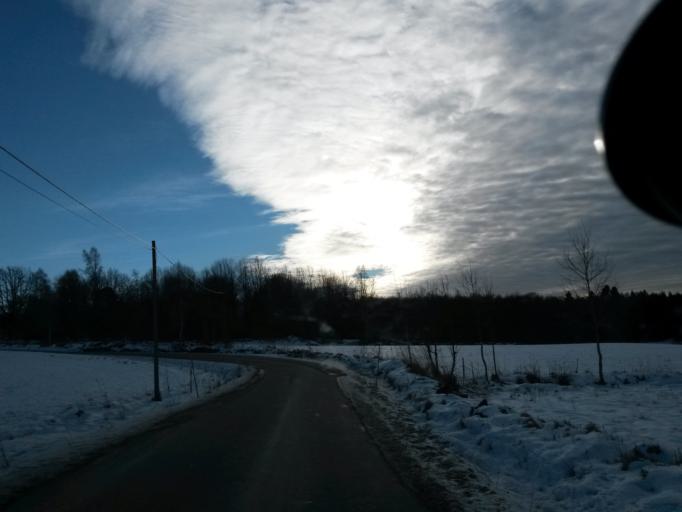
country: SE
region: Vaestra Goetaland
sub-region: Vargarda Kommun
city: Vargarda
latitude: 58.0081
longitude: 12.8828
